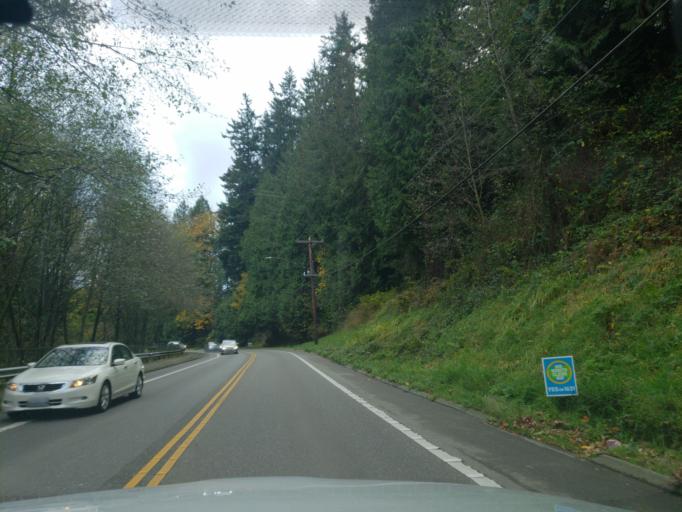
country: US
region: Washington
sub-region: Snohomish County
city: Everett
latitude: 47.9590
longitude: -122.2274
